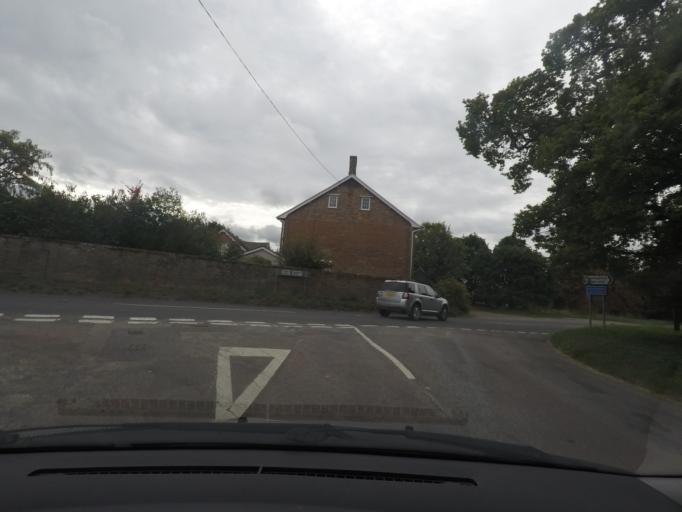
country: GB
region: England
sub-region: Wiltshire
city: Pewsey
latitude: 51.3211
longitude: -1.7978
